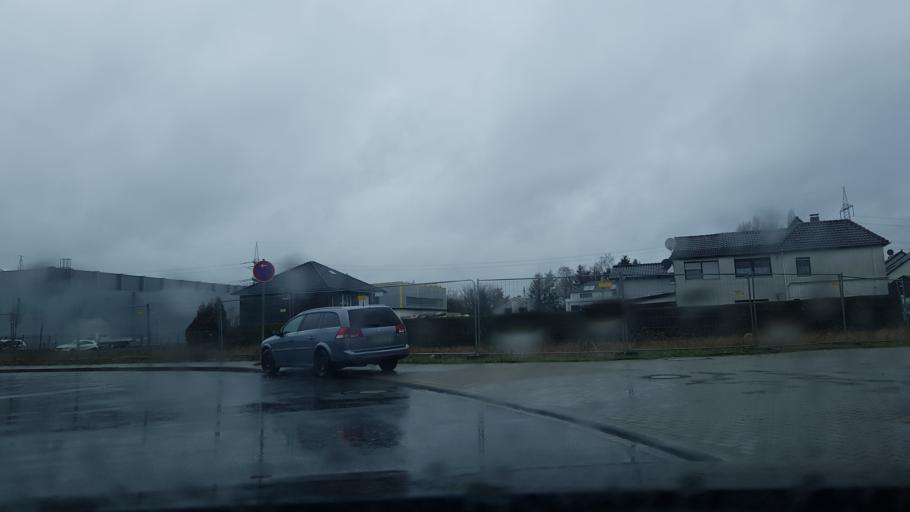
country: DE
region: North Rhine-Westphalia
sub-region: Regierungsbezirk Dusseldorf
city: Langenfeld
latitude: 51.1230
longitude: 6.9207
